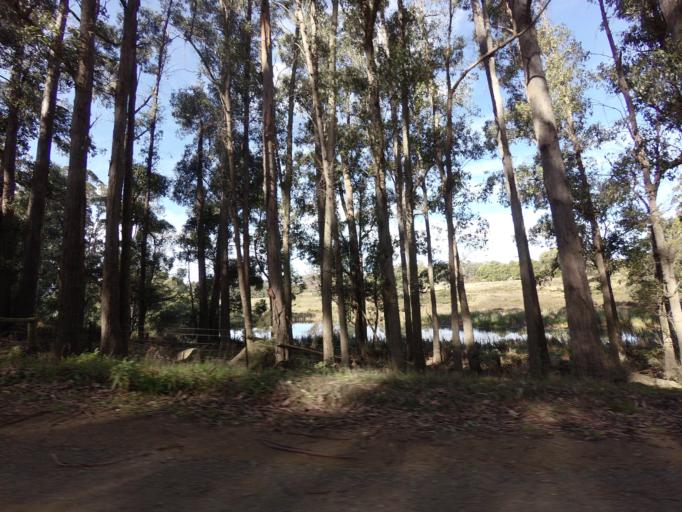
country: AU
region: Tasmania
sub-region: Clarence
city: Sandford
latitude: -43.1522
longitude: 147.7633
